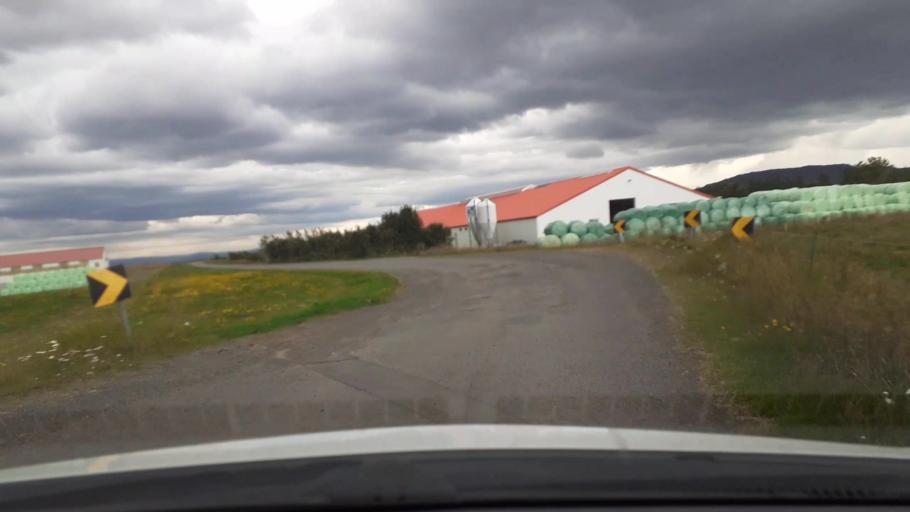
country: IS
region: West
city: Borgarnes
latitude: 64.5676
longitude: -21.7588
